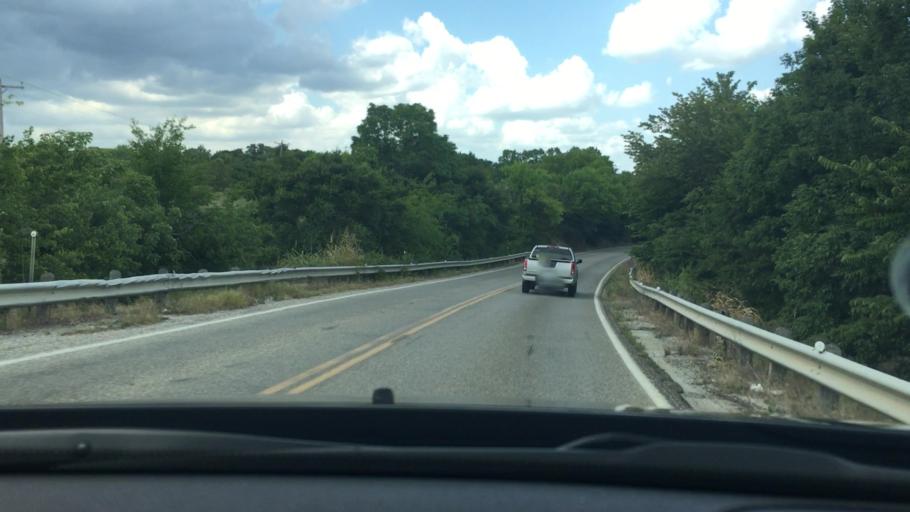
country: US
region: Oklahoma
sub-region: Pontotoc County
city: Ada
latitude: 34.5654
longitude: -96.6345
